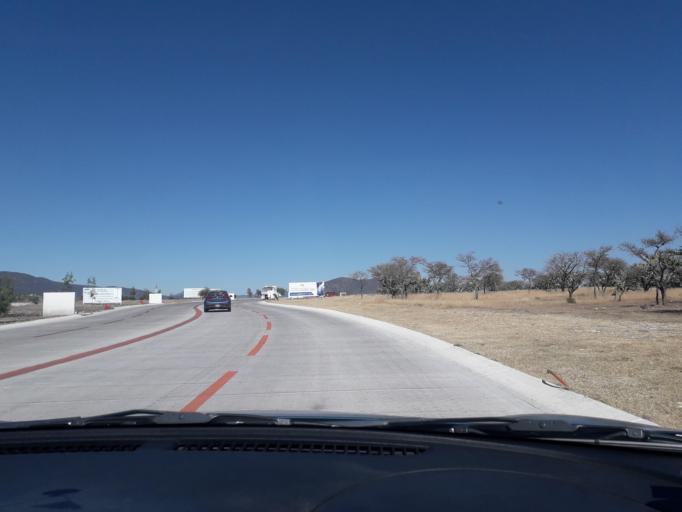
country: MX
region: Queretaro
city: Santa Rosa Jauregui
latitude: 20.7337
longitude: -100.4823
